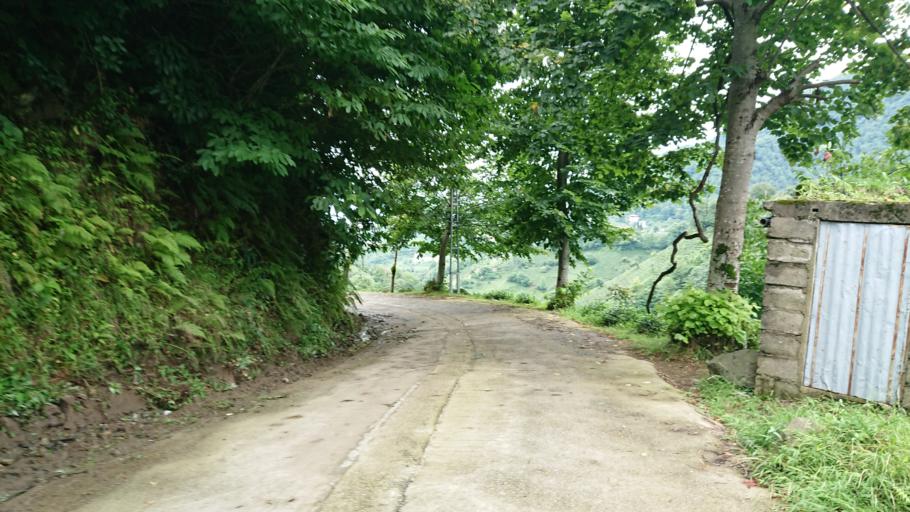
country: TR
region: Rize
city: Rize
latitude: 40.9754
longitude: 40.4856
